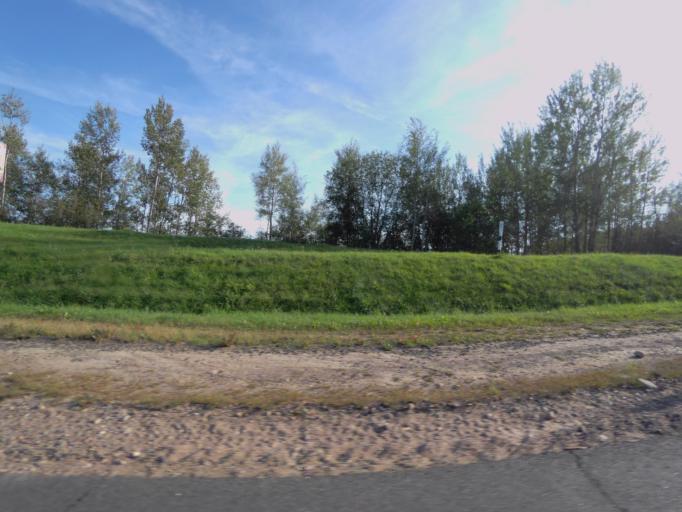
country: BY
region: Minsk
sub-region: Smalyavitski Rayon
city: Usjazh
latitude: 54.0297
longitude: 27.9888
